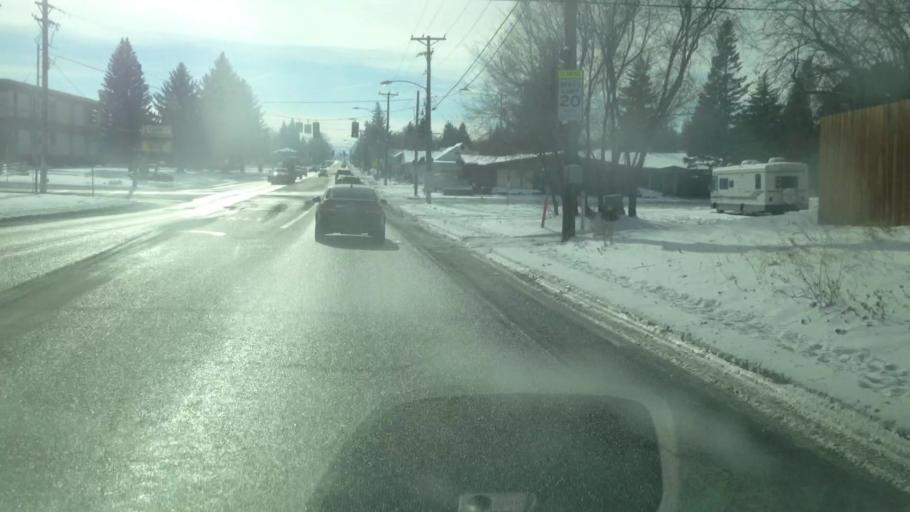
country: US
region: Idaho
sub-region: Bonneville County
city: Idaho Falls
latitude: 43.4943
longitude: -112.0239
